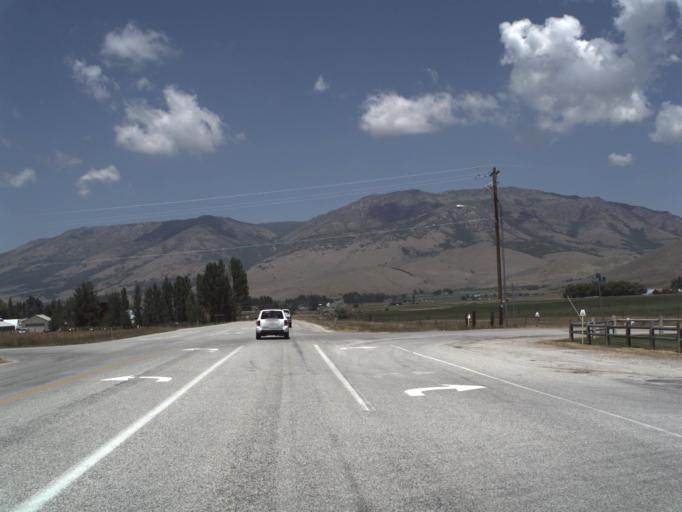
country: US
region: Utah
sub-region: Weber County
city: Wolf Creek
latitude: 41.2525
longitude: -111.7611
